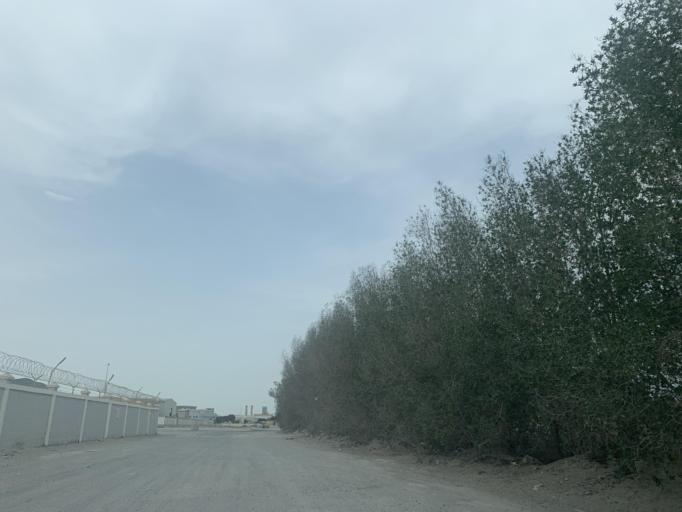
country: BH
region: Muharraq
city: Al Hadd
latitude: 26.2061
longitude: 50.6699
